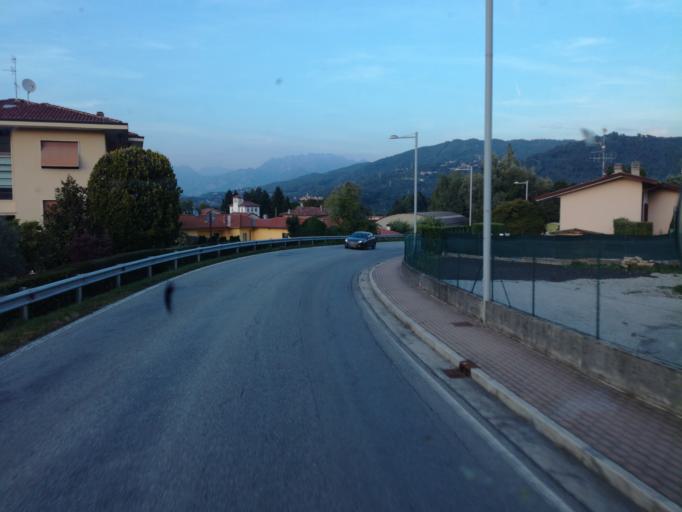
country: IT
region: Lombardy
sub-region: Provincia di Lecco
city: Sirtori
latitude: 45.7484
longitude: 9.3282
